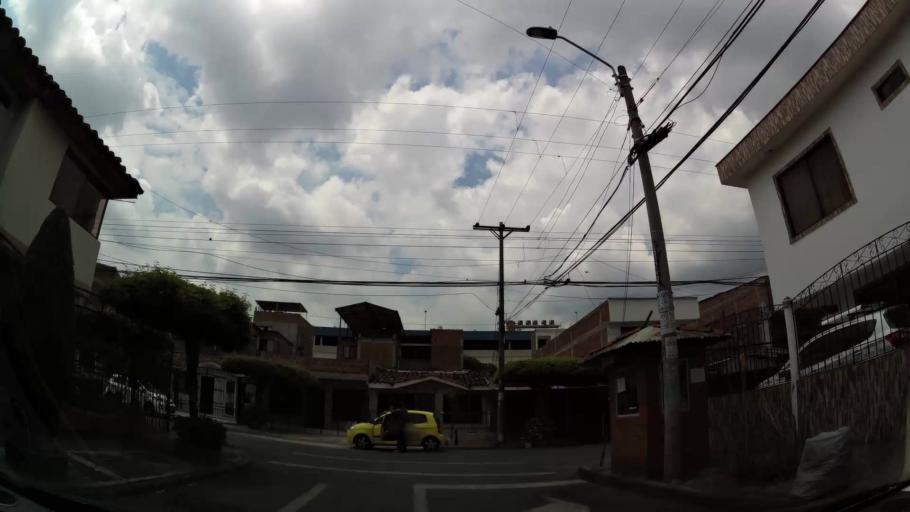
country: CO
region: Valle del Cauca
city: Cali
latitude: 3.4657
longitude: -76.4989
